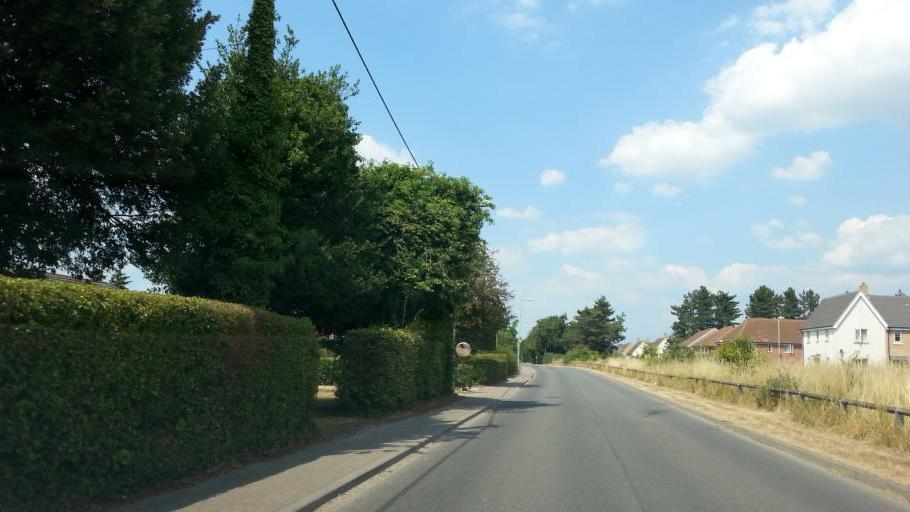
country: GB
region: England
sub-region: Cambridgeshire
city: Isleham
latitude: 52.3014
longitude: 0.4946
